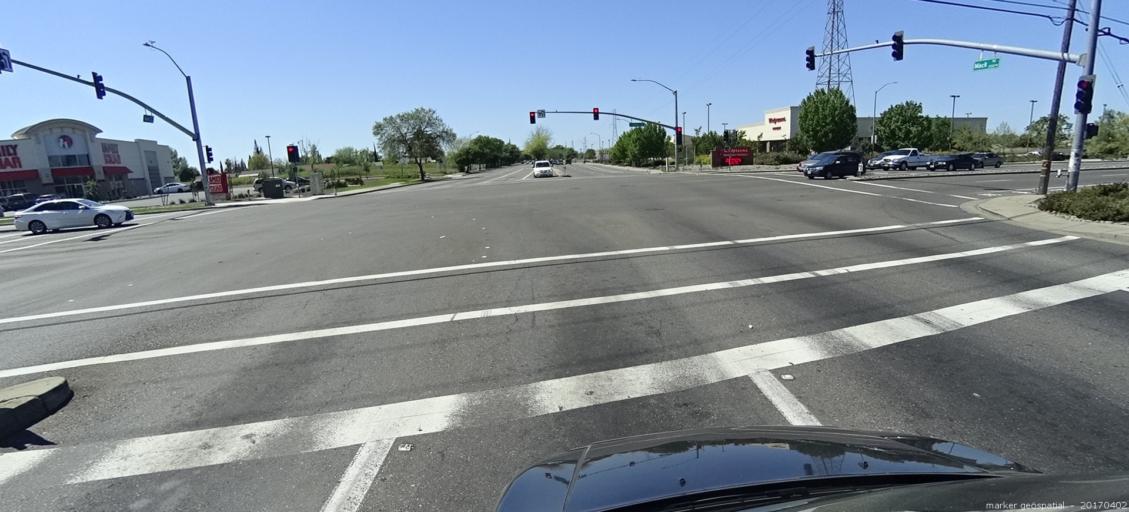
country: US
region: California
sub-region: Sacramento County
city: Parkway
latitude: 38.4743
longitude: -121.4500
